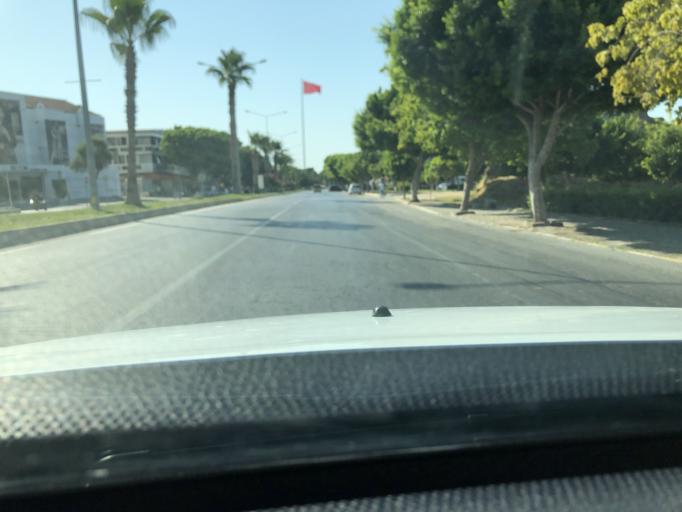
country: TR
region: Antalya
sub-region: Manavgat
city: Side
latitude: 36.7789
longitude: 31.3953
